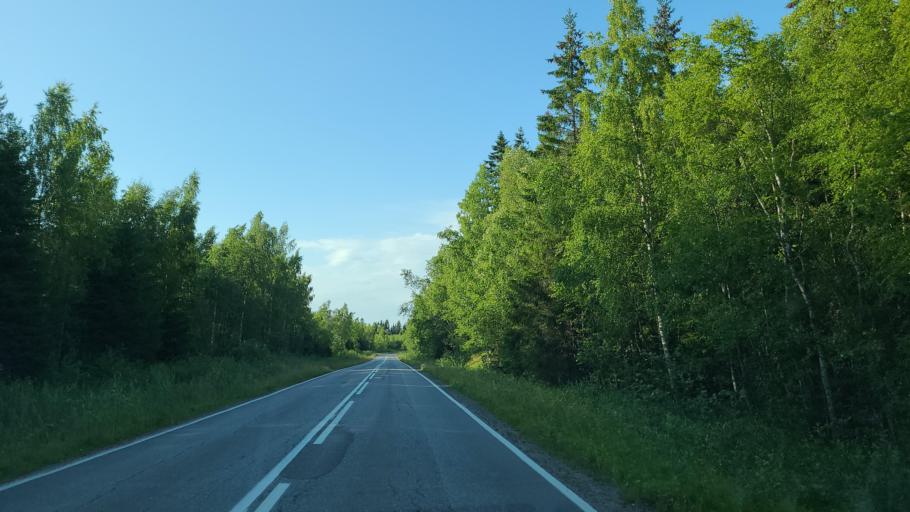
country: FI
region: Ostrobothnia
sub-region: Vaasa
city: Replot
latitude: 63.3009
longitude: 21.3592
